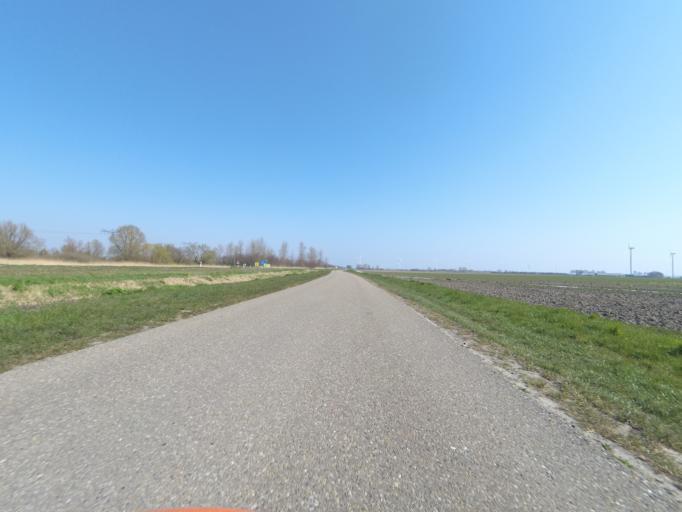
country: NL
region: Utrecht
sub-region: Gemeente Bunschoten
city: Spakenburg
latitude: 52.3065
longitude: 5.3433
